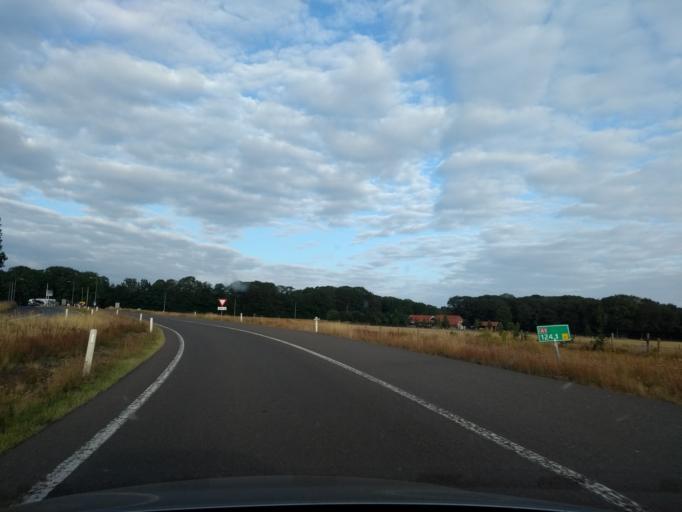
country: NL
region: Overijssel
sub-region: Gemeente Hof van Twente
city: Markelo
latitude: 52.2650
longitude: 6.4579
